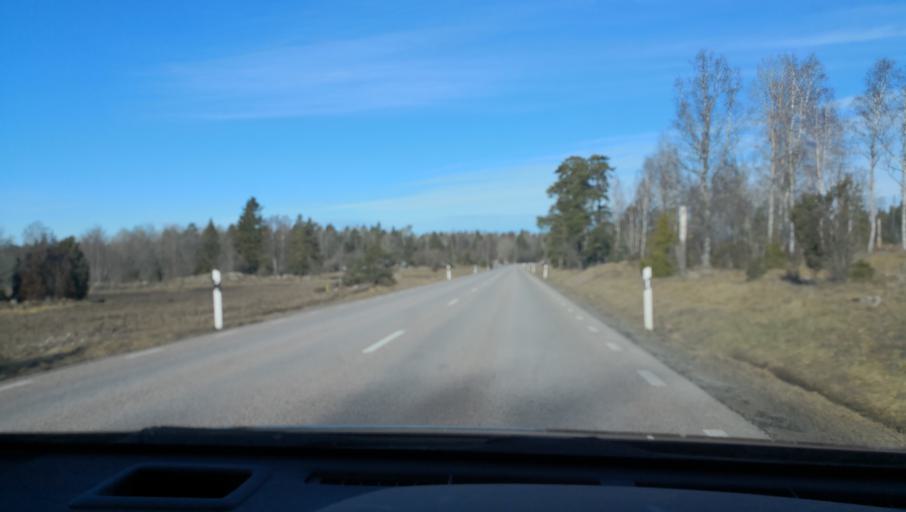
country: SE
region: Uppsala
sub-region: Uppsala Kommun
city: Vattholma
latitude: 60.0923
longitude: 17.7702
